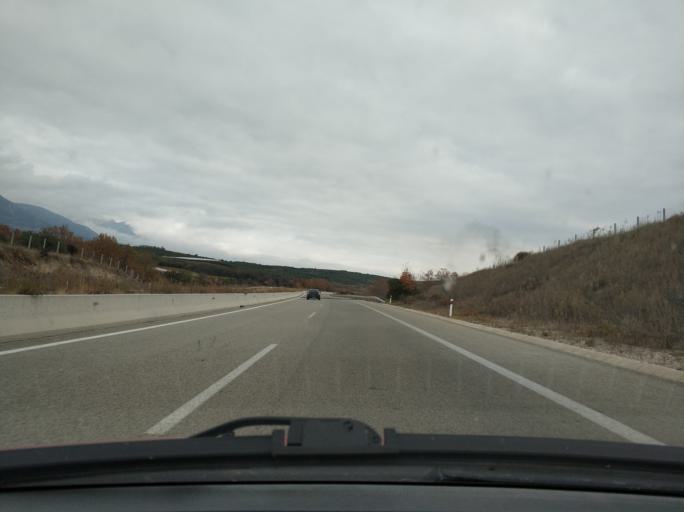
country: GR
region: East Macedonia and Thrace
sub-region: Nomos Kavalas
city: Paralia Ofryniou
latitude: 40.7905
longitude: 23.9729
